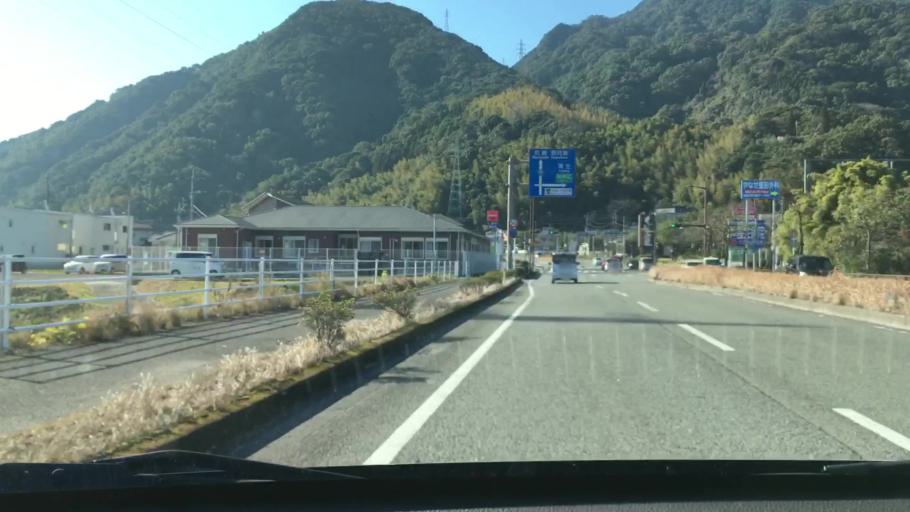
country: JP
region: Kagoshima
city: Kajiki
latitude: 31.7053
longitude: 130.6129
